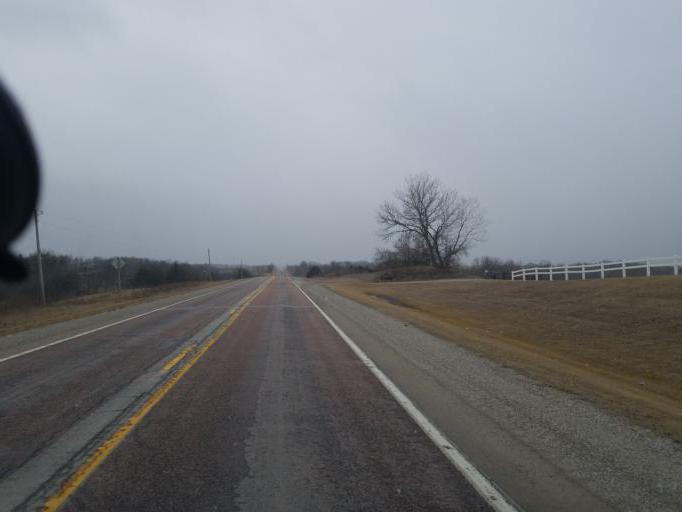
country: US
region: Iowa
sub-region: Appanoose County
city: Centerville
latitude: 40.6280
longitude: -92.9445
